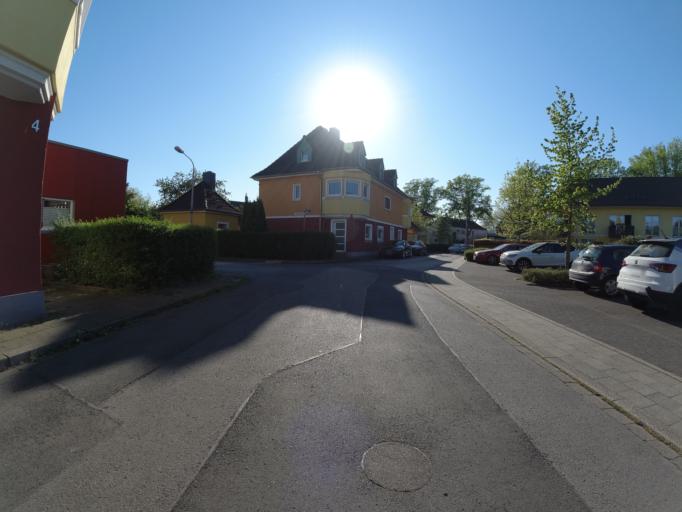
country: DE
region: North Rhine-Westphalia
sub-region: Regierungsbezirk Dusseldorf
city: Hochfeld
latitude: 51.3874
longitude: 6.7064
